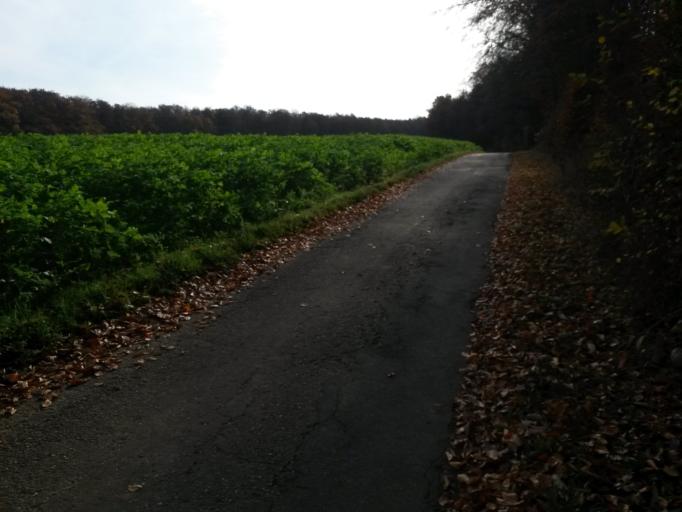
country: DE
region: Baden-Wuerttemberg
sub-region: Karlsruhe Region
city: Neuenburg
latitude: 48.8895
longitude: 8.5797
